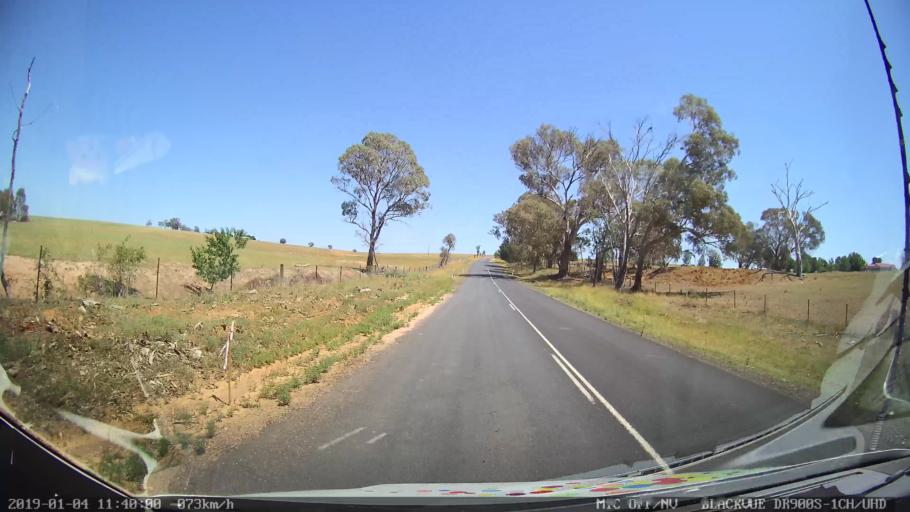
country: AU
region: New South Wales
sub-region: Cabonne
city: Molong
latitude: -33.0085
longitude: 148.7906
